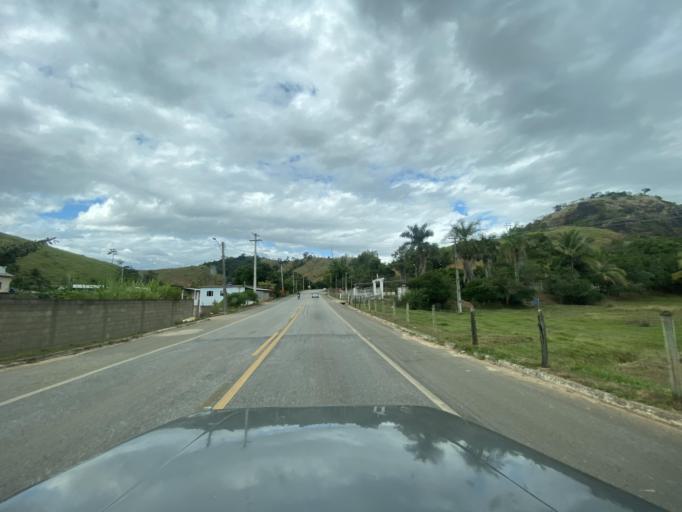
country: BR
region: Espirito Santo
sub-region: Jeronimo Monteiro
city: Jeronimo Monteiro
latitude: -20.7630
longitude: -41.4500
